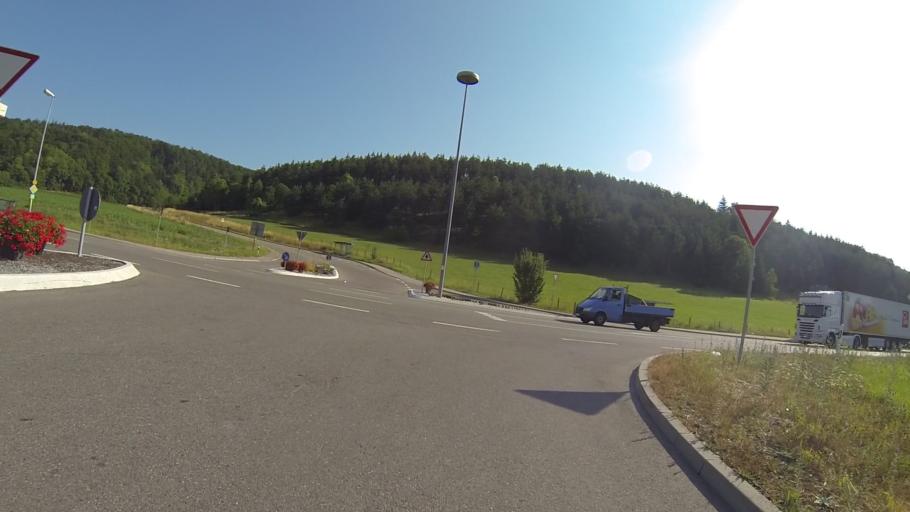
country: DE
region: Baden-Wuerttemberg
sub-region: Regierungsbezirk Stuttgart
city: Konigsbronn
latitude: 48.7335
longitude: 10.1379
